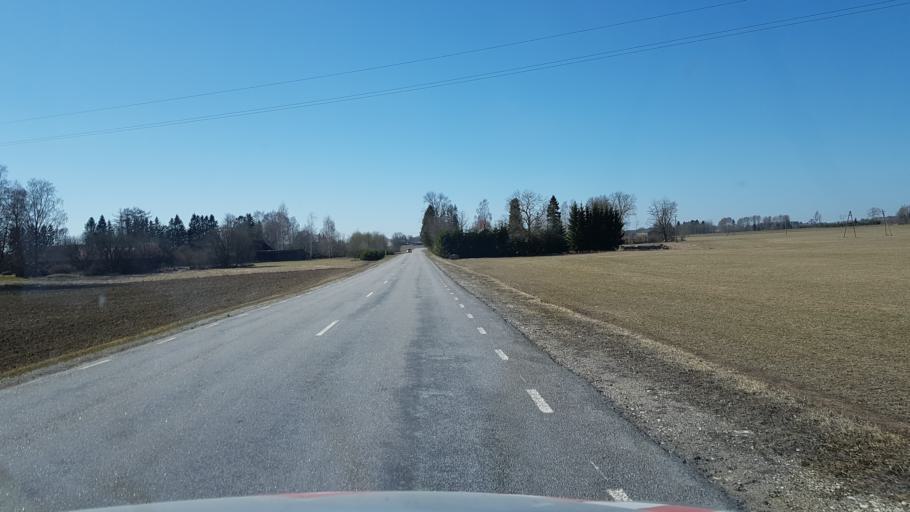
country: EE
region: Laeaene-Virumaa
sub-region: Tamsalu vald
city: Tamsalu
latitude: 59.1689
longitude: 26.1584
